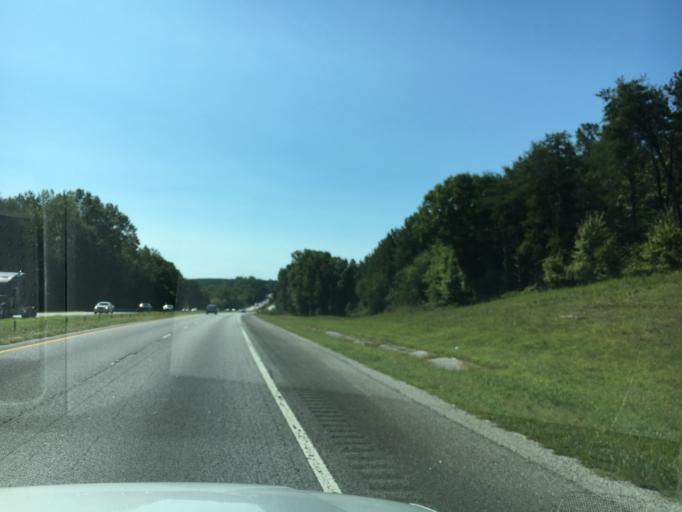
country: US
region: South Carolina
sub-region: Spartanburg County
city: Roebuck
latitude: 34.7962
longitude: -81.9577
